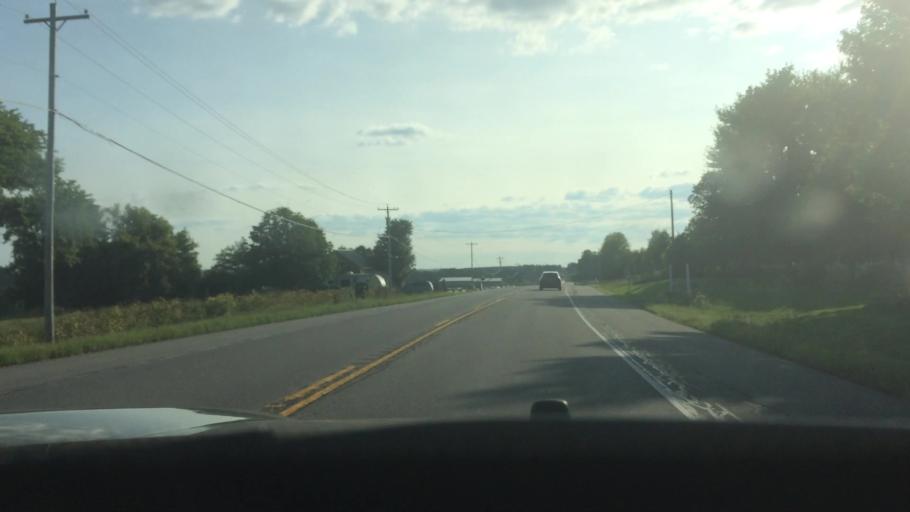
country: US
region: New York
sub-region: St. Lawrence County
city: Canton
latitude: 44.6172
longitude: -75.1068
